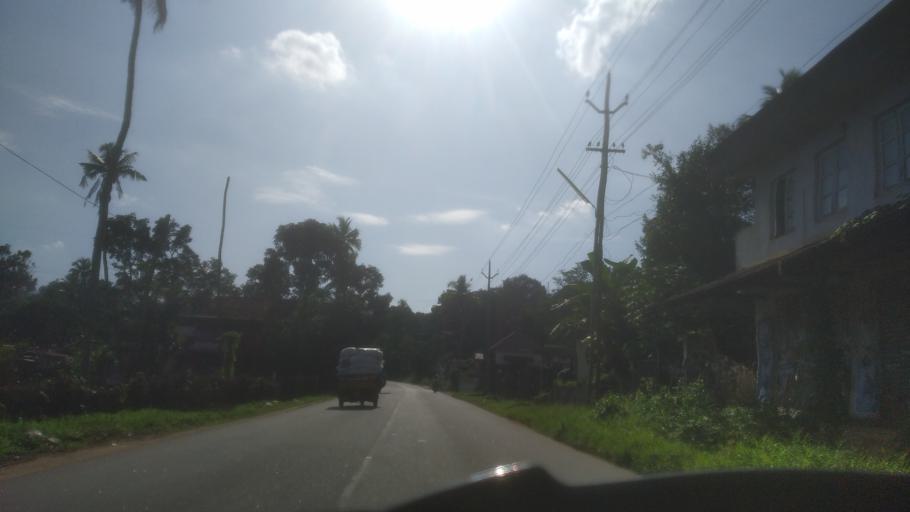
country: IN
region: Kerala
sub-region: Ernakulam
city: Muvattupuzha
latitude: 9.9841
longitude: 76.5611
